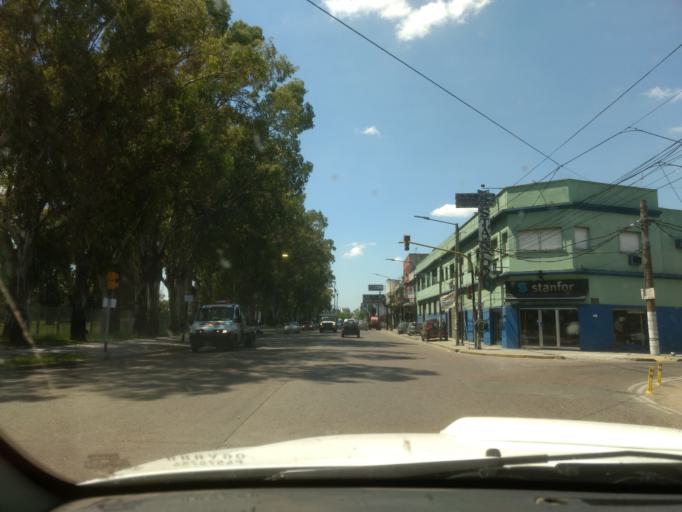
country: AR
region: Buenos Aires
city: Caseros
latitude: -34.6164
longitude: -58.5391
